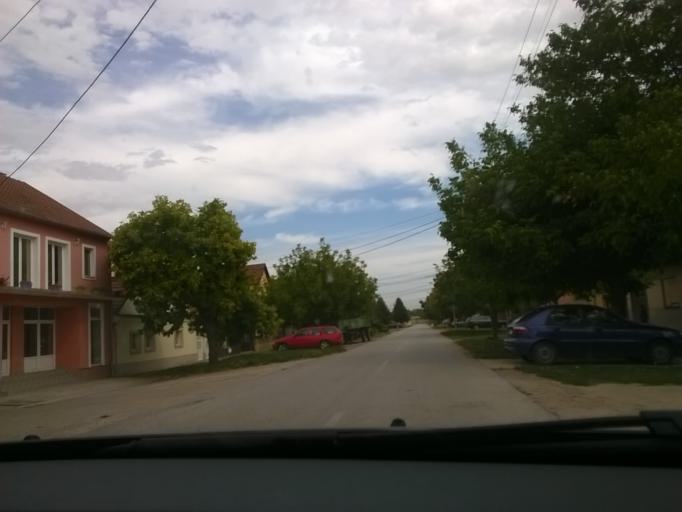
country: RS
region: Autonomna Pokrajina Vojvodina
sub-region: Juznobanatski Okrug
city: Vrsac
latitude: 45.1278
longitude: 21.2924
